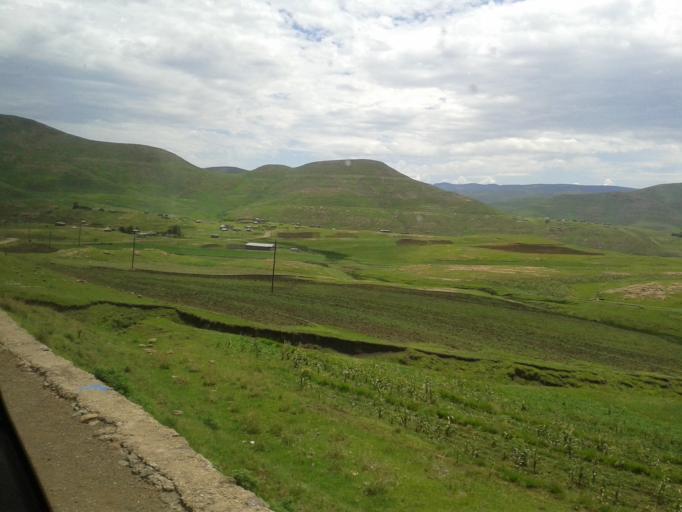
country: LS
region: Maseru
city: Nako
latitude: -29.8453
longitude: 28.0257
